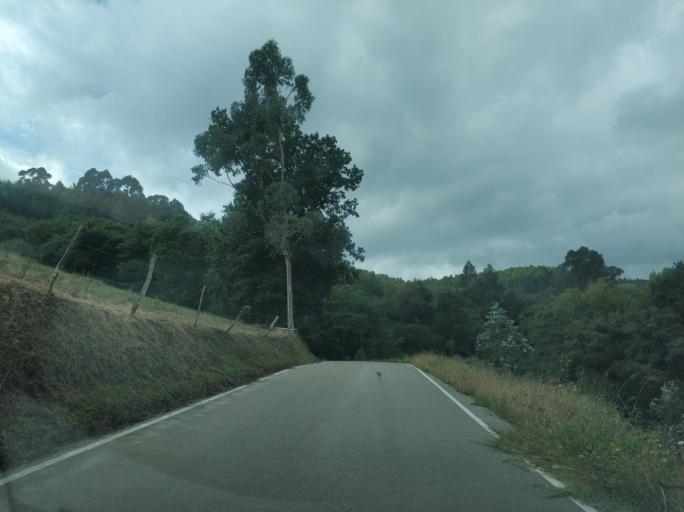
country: ES
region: Cantabria
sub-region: Provincia de Cantabria
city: San Miguel de Meruelo
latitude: 43.4329
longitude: -3.5758
